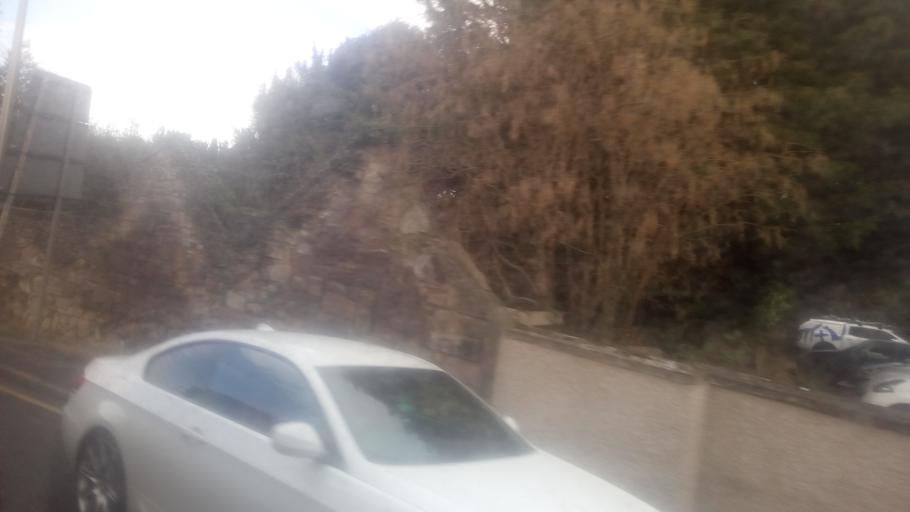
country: GB
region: Scotland
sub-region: Midlothian
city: Dalkeith
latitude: 55.8949
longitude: -3.0702
